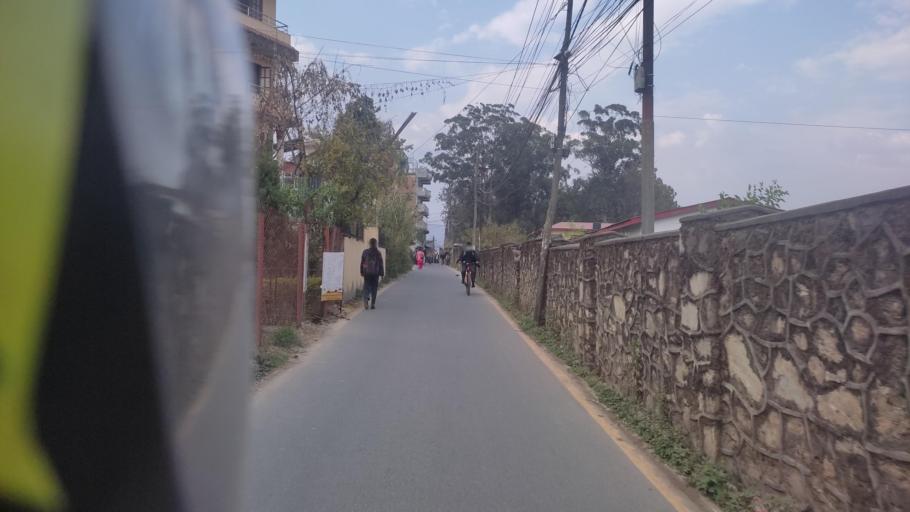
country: NP
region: Central Region
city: Kirtipur
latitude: 27.6795
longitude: 85.2816
